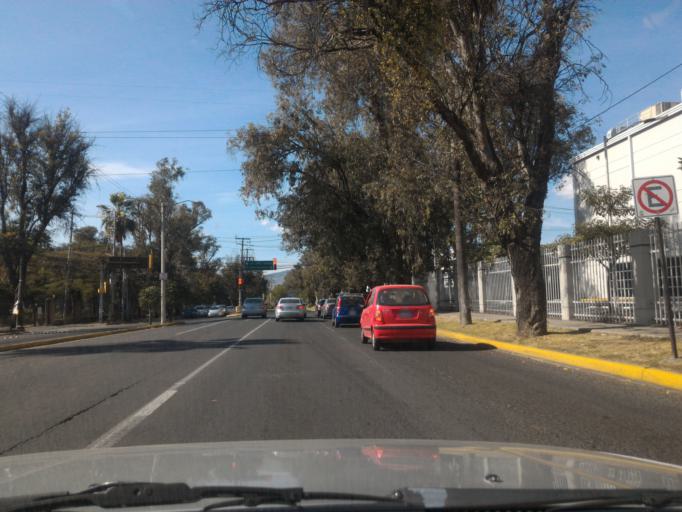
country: MX
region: Jalisco
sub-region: Tlajomulco de Zuniga
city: La Tijera
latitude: 20.6155
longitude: -103.4201
